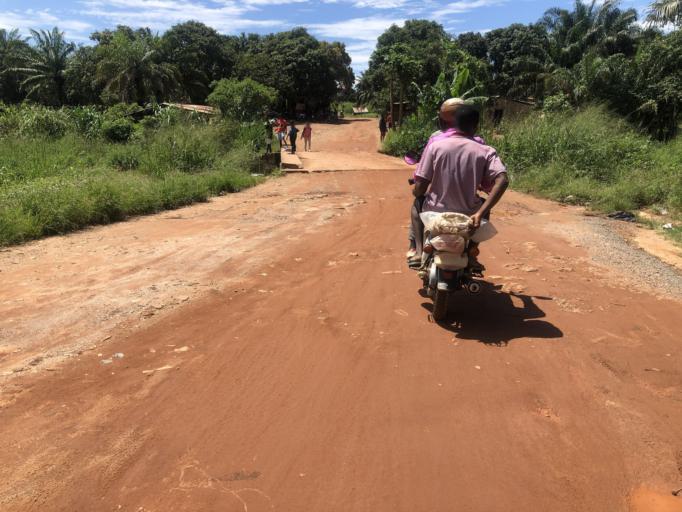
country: SL
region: Eastern Province
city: Koidu
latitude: 8.6440
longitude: -10.9626
